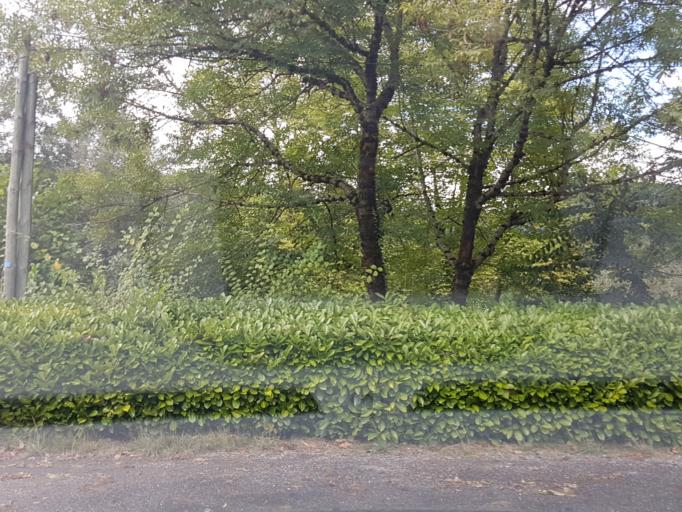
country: FR
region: Midi-Pyrenees
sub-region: Departement de l'Ariege
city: Saint-Girons
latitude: 42.8923
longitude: 1.2143
